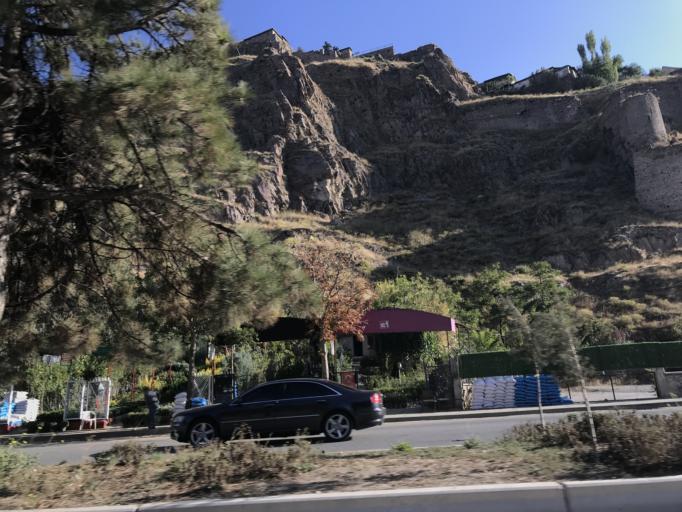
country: TR
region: Ankara
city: Cankaya
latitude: 39.9433
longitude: 32.8647
